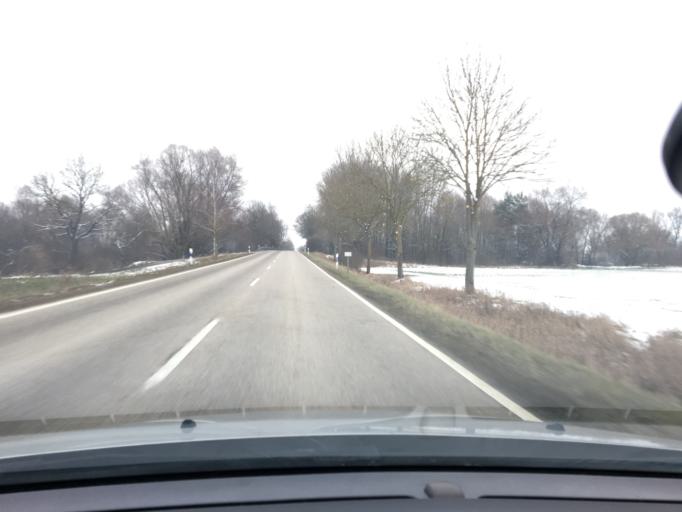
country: DE
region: Bavaria
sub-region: Upper Bavaria
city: Moosburg
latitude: 48.4660
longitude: 11.9085
